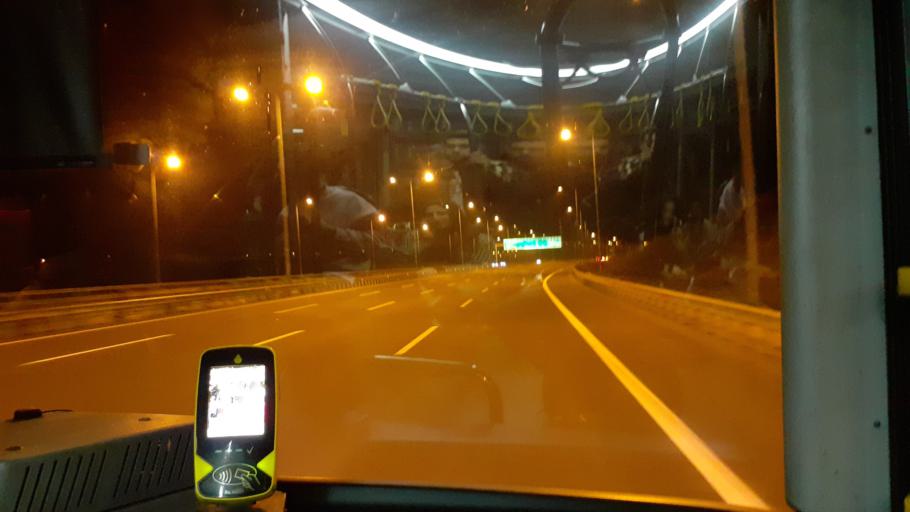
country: TR
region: Istanbul
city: Kemerburgaz
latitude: 41.2376
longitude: 28.8301
